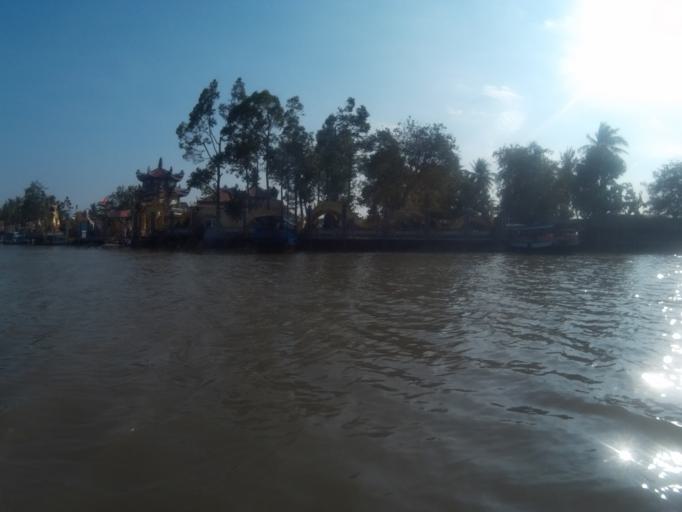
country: VN
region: Dong Nai
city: Bien Hoa
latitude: 10.8804
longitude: 106.8462
